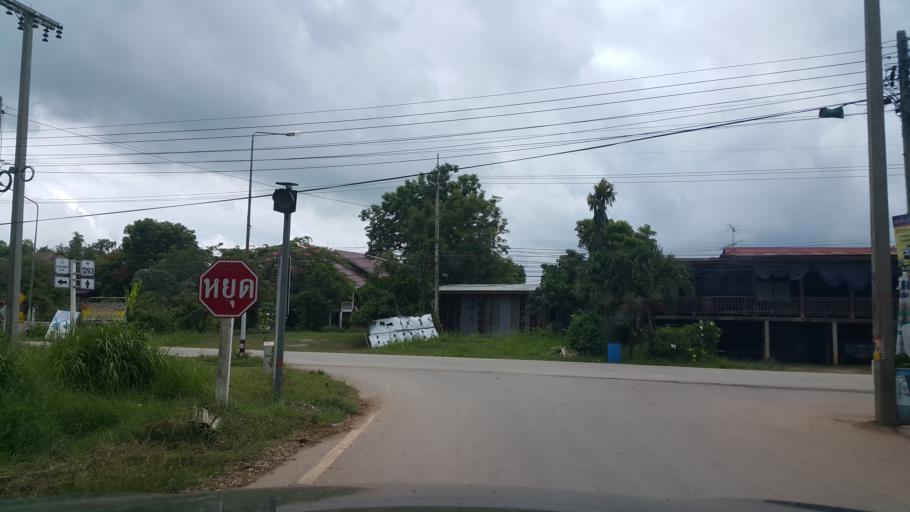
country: TH
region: Sukhothai
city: Kong Krailat
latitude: 16.9049
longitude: 99.8816
